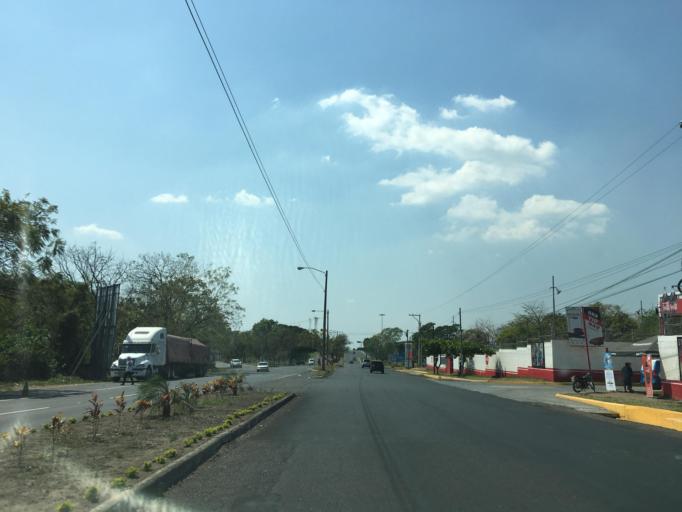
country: GT
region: Escuintla
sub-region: Municipio de Escuintla
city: Escuintla
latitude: 14.2926
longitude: -90.7969
